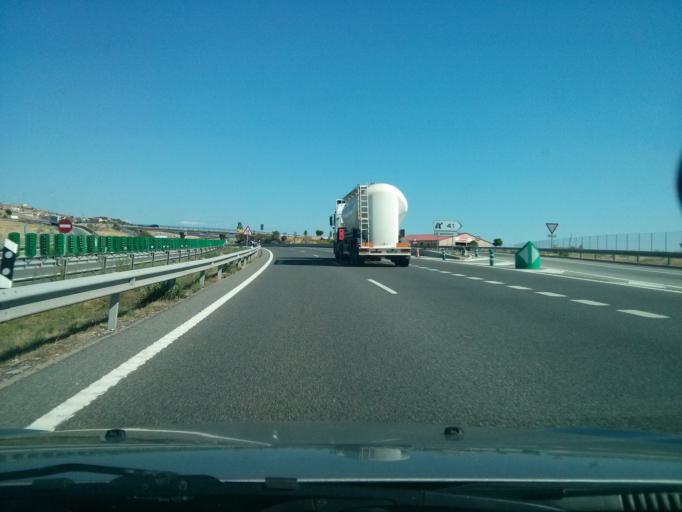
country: ES
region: Madrid
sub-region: Provincia de Madrid
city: El Molar
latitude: 40.7143
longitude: -3.5776
